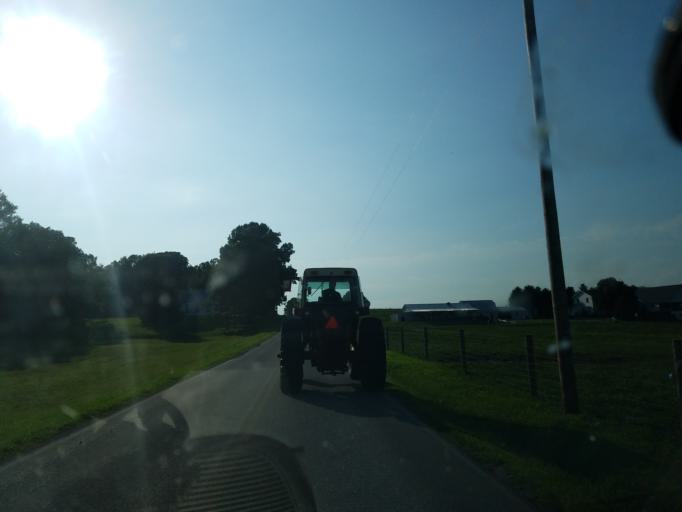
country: US
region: Ohio
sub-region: Adams County
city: West Union
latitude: 38.8862
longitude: -83.5066
